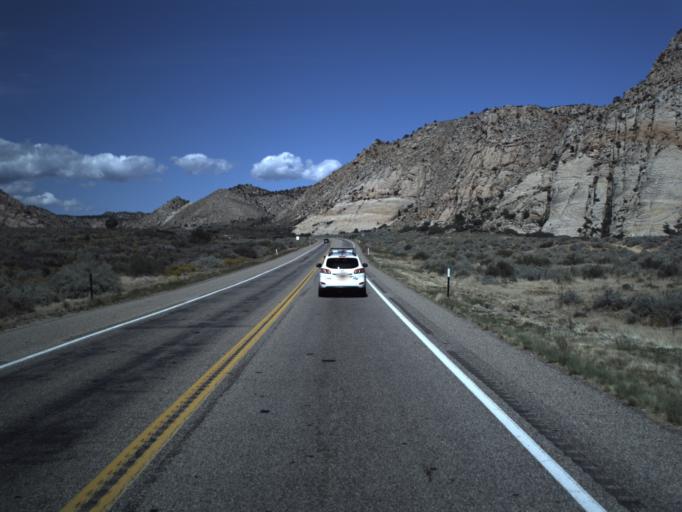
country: US
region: Utah
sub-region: Washington County
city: Ivins
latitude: 37.2261
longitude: -113.6335
